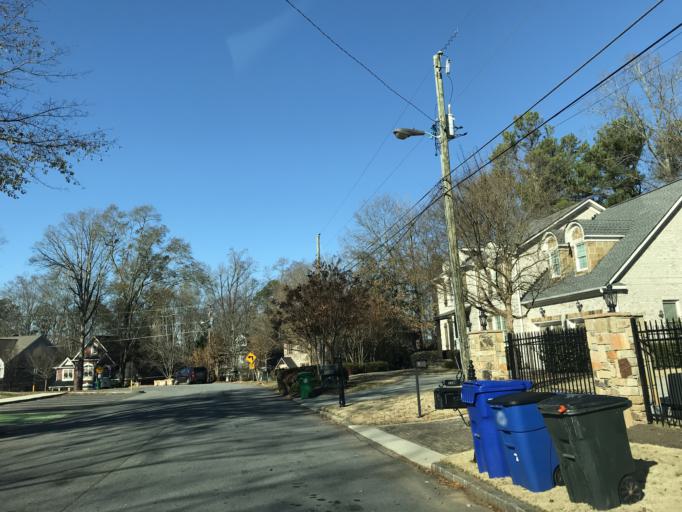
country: US
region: Georgia
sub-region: DeKalb County
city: North Atlanta
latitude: 33.8885
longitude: -84.3458
